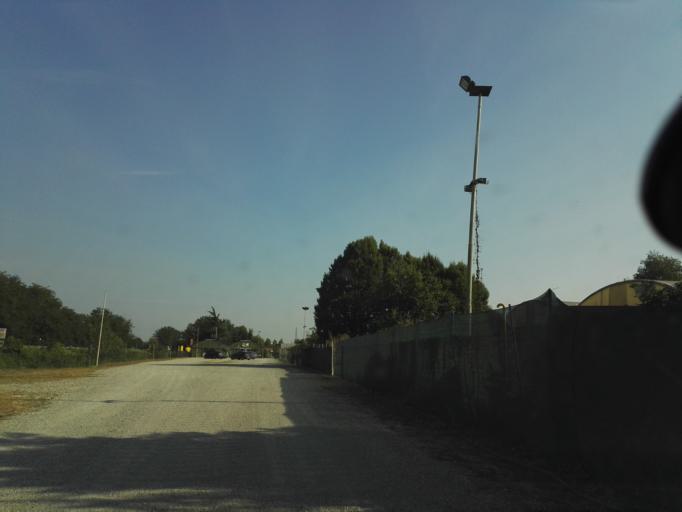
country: IT
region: Lombardy
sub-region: Citta metropolitana di Milano
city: San Giuliano Milanese
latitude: 45.3765
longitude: 9.3052
